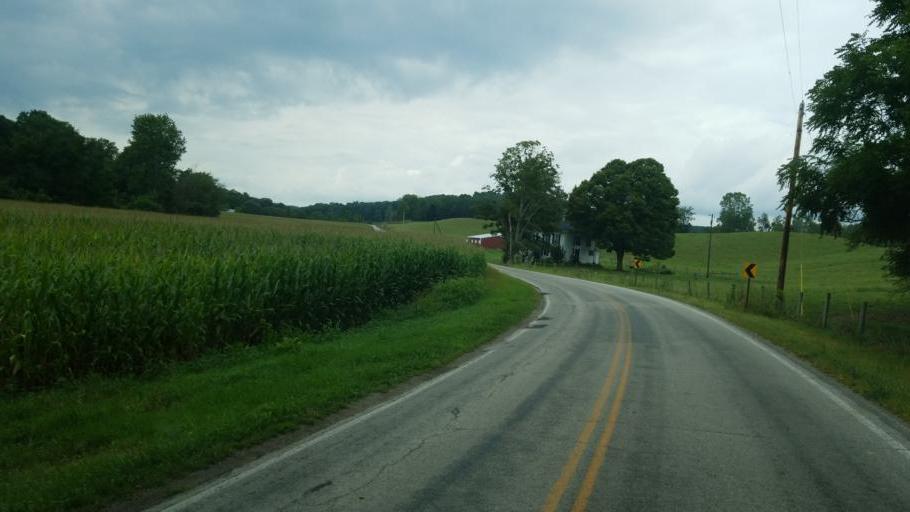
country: US
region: Ohio
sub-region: Sandusky County
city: Bellville
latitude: 40.6296
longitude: -82.3958
